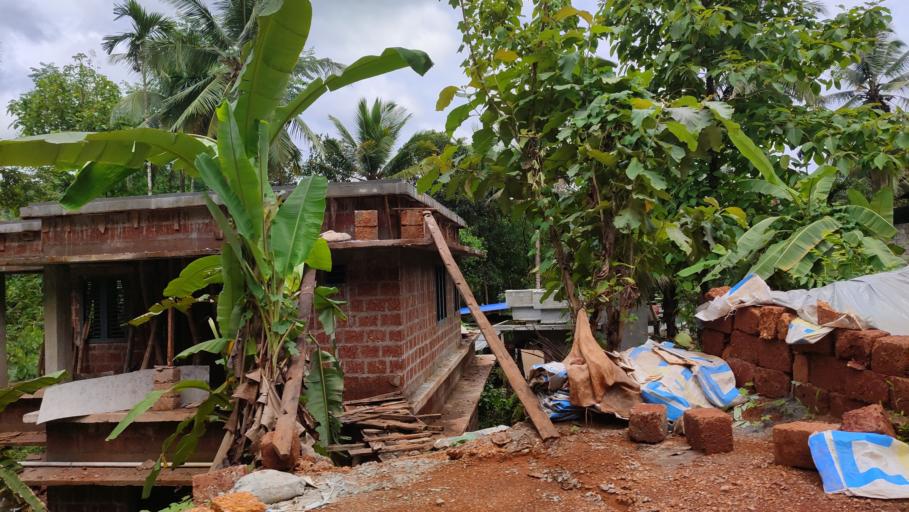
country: IN
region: Kerala
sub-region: Kasaragod District
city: Nileshwar
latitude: 12.2937
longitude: 75.2741
